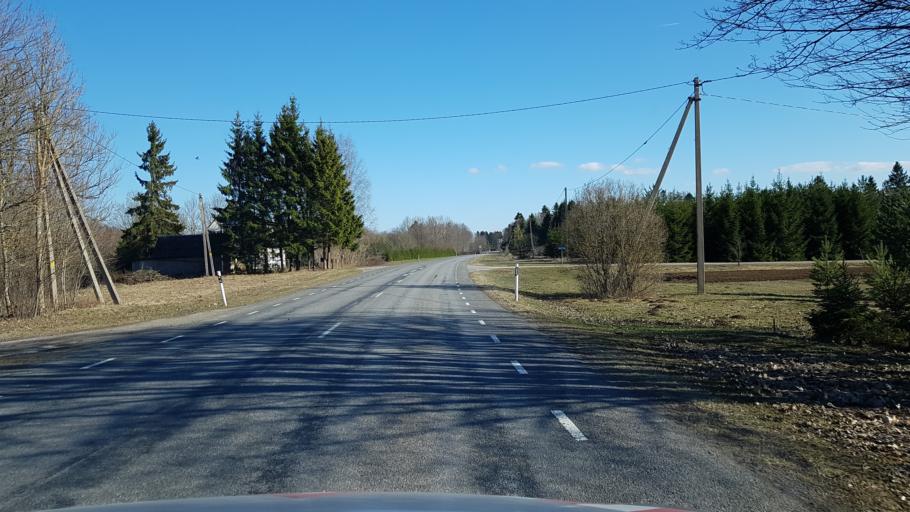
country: EE
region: Laeaene-Virumaa
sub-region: Haljala vald
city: Haljala
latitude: 59.4471
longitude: 26.2495
